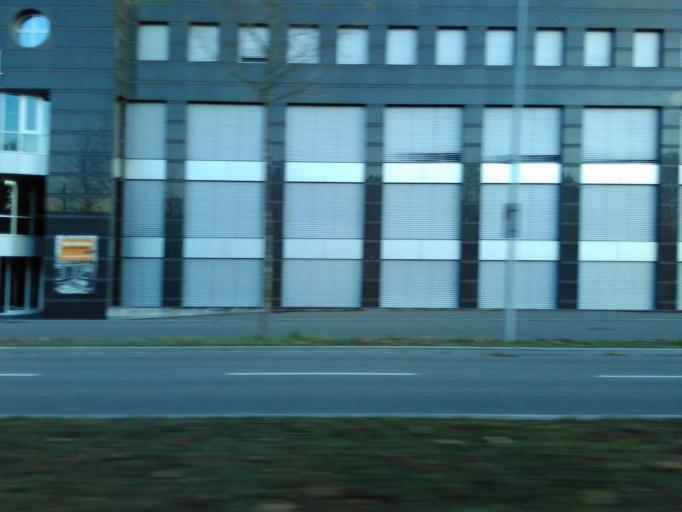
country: CH
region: Zurich
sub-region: Bezirk Zuerich
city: Zuerich (Kreis 11) / Seebach
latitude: 47.4157
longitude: 8.5525
